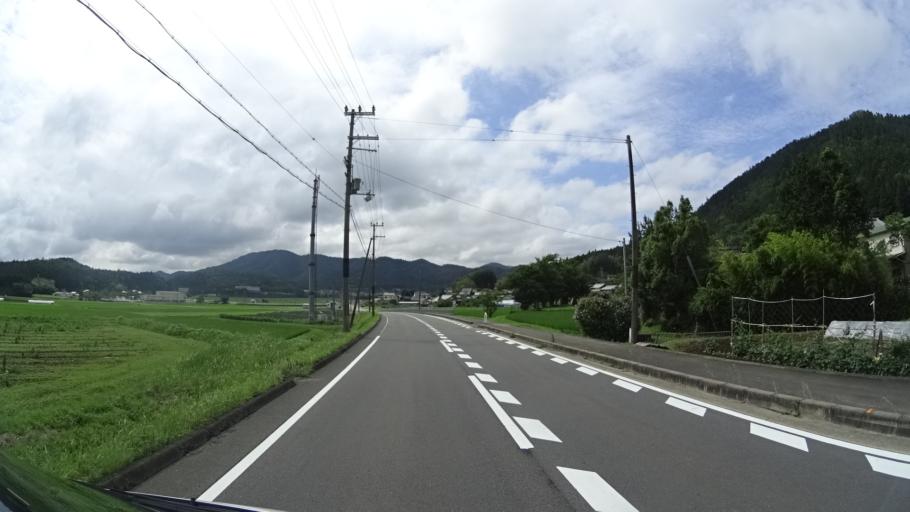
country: JP
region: Kyoto
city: Kameoka
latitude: 35.0269
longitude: 135.4844
